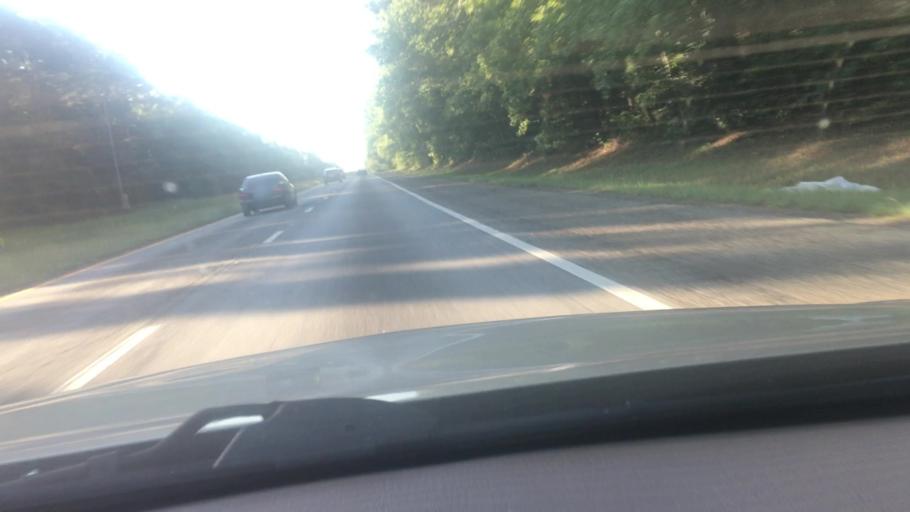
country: US
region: South Carolina
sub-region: Lexington County
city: Irmo
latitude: 34.1295
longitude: -81.2065
